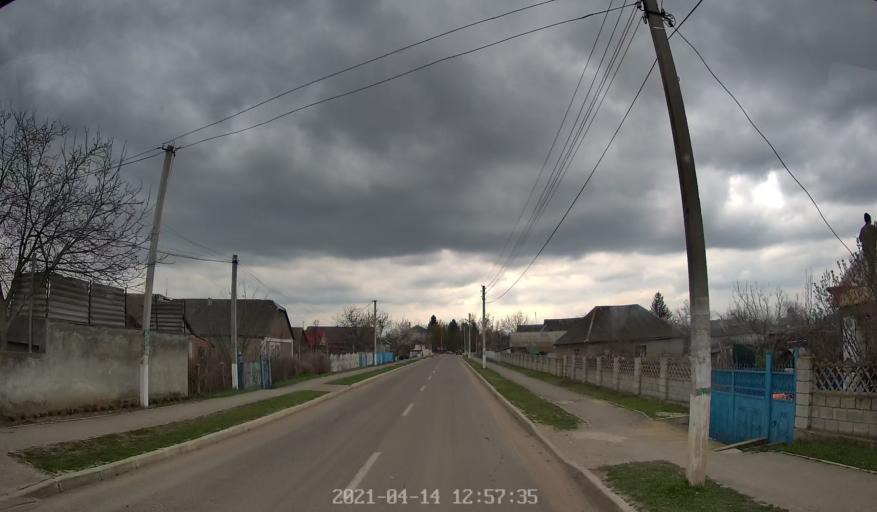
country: MD
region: Criuleni
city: Criuleni
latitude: 47.1503
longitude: 29.1407
